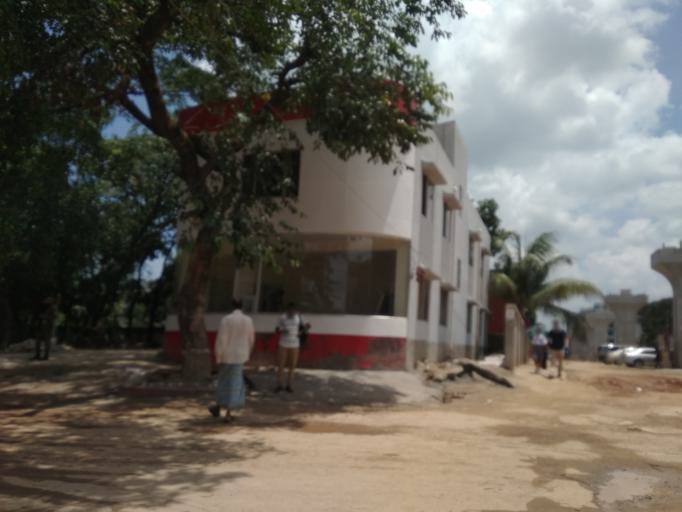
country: BD
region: Dhaka
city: Tungi
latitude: 23.8320
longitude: 90.3637
